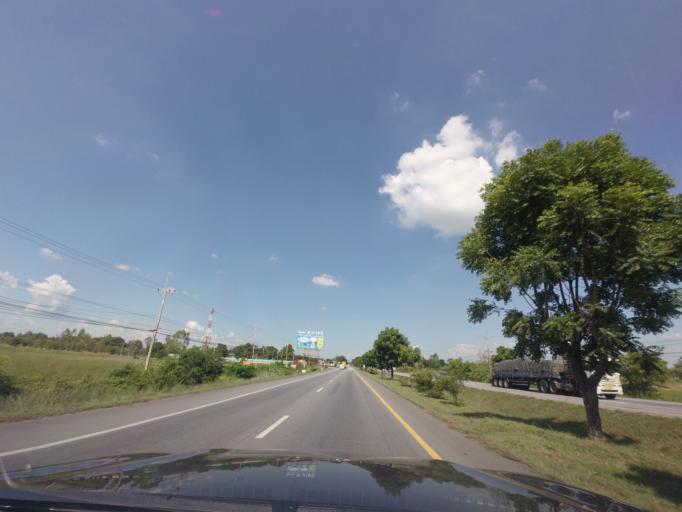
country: TH
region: Nakhon Ratchasima
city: Non Sung
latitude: 15.1419
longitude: 102.3169
